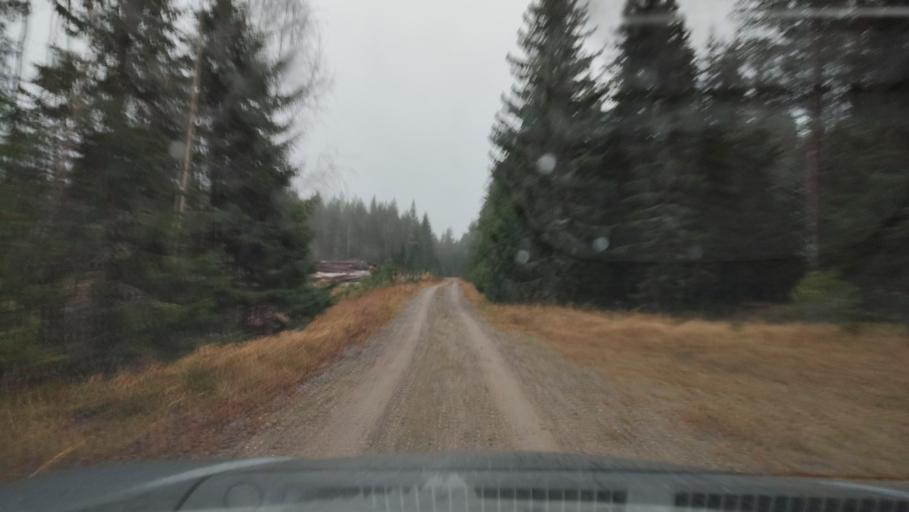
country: FI
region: Southern Ostrobothnia
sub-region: Suupohja
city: Karijoki
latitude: 62.1816
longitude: 21.7317
